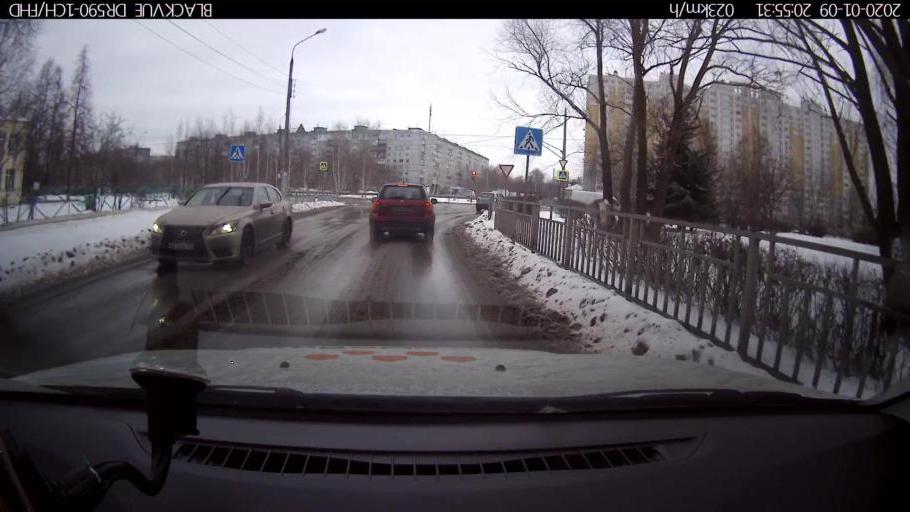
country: RU
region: Nizjnij Novgorod
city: Nizhniy Novgorod
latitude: 56.2841
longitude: 43.9431
